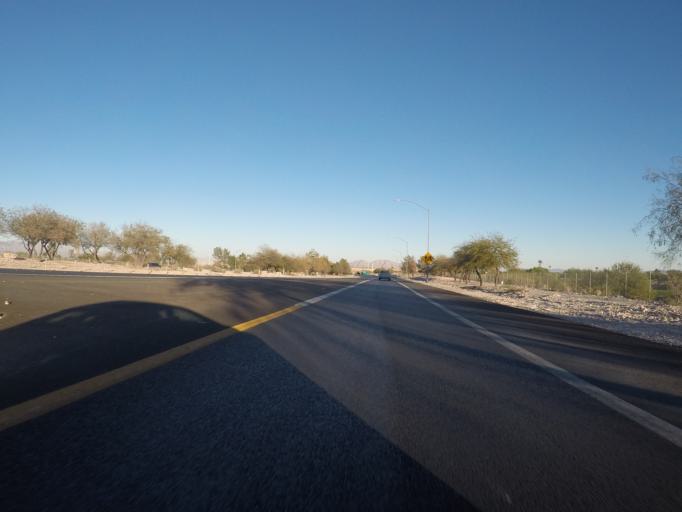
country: US
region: Nevada
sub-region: Clark County
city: Summerlin South
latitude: 36.1772
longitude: -115.2840
